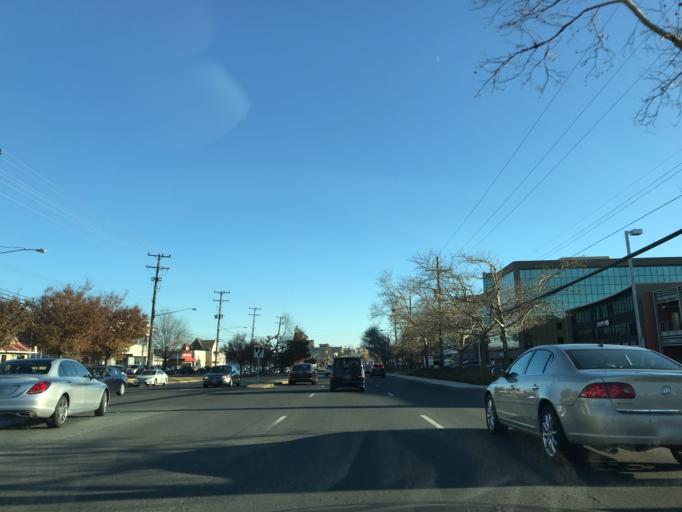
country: US
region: Maryland
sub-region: Montgomery County
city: North Bethesda
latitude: 39.0686
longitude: -77.1299
